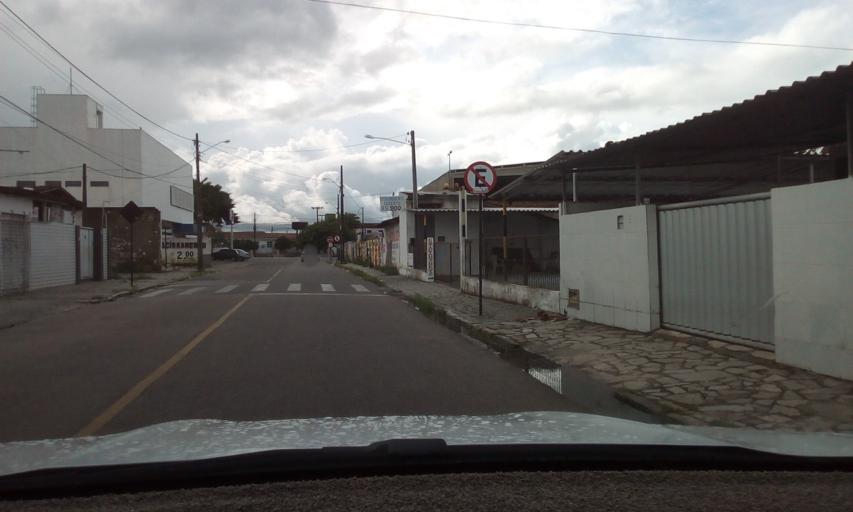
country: BR
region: Paraiba
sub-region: Joao Pessoa
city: Joao Pessoa
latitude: -7.1378
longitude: -34.8860
